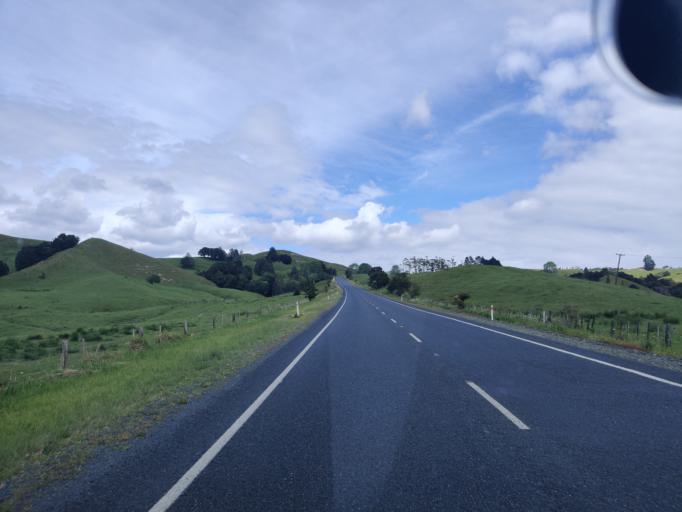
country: NZ
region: Northland
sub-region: Far North District
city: Taipa
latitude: -35.0523
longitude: 173.6804
